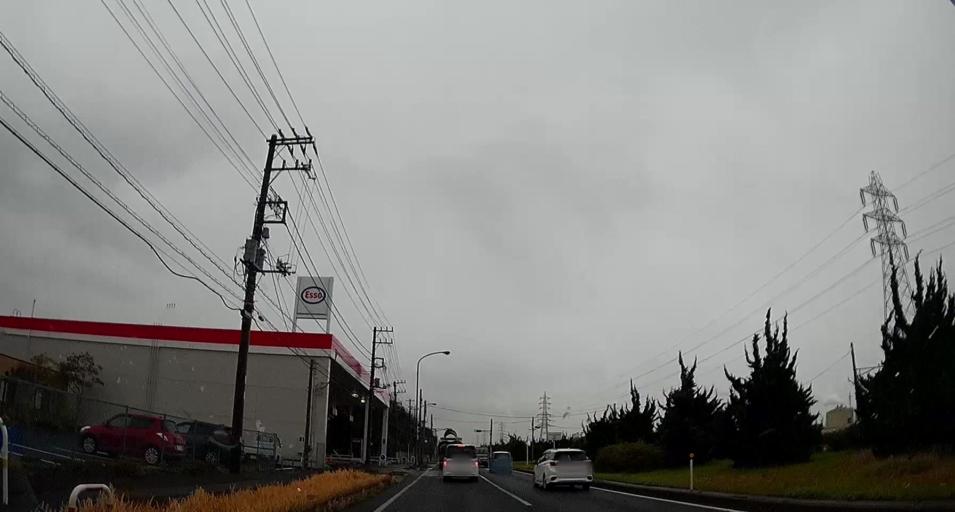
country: JP
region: Chiba
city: Ichihara
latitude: 35.5126
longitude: 140.0570
